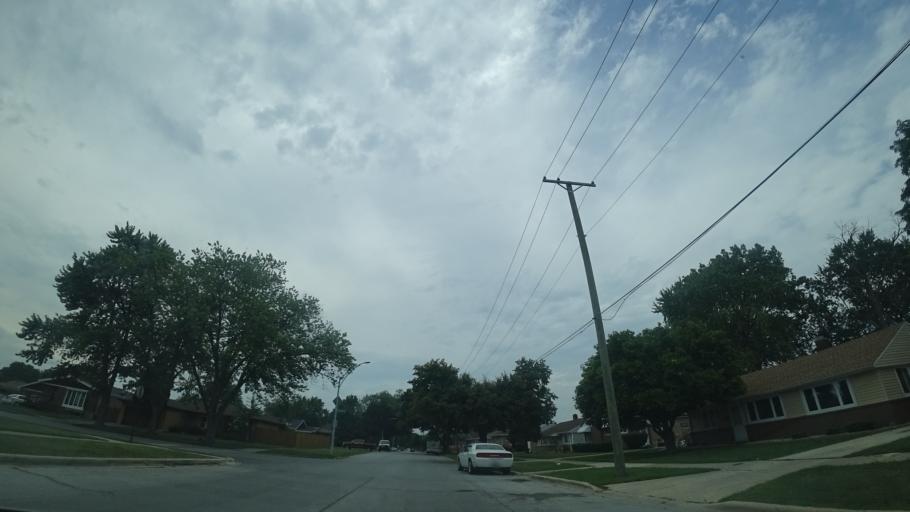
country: US
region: Illinois
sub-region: Cook County
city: Merrionette Park
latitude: 41.6986
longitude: -87.7214
